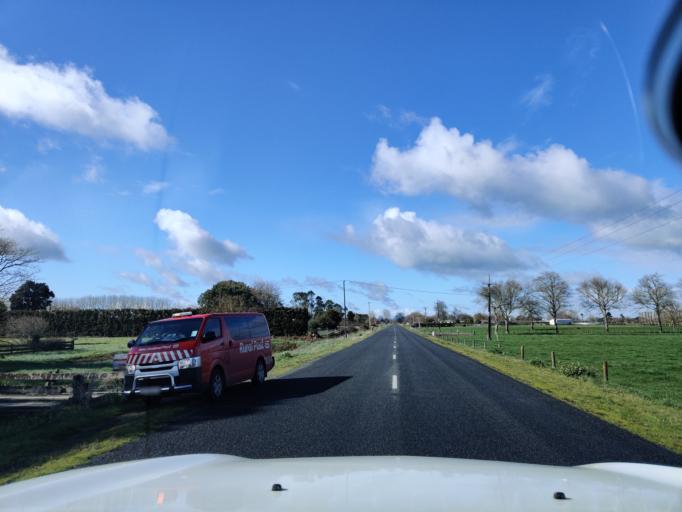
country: NZ
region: Waikato
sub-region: Waikato District
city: Ngaruawahia
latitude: -37.6043
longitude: 175.3037
